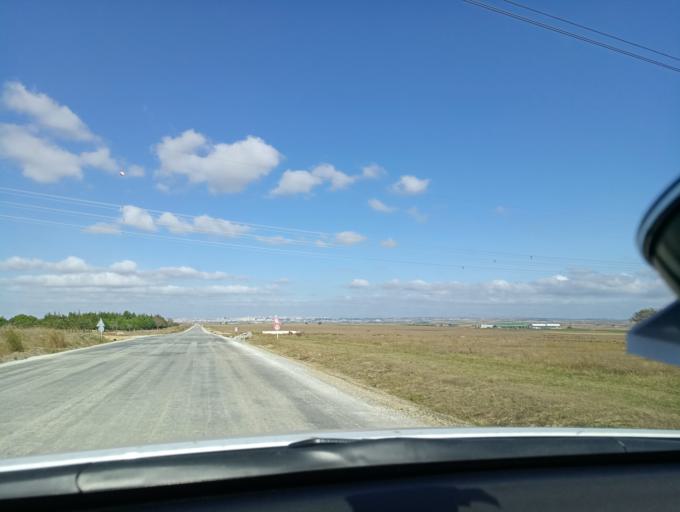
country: TR
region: Tekirdag
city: Corlu
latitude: 41.0606
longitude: 27.8344
